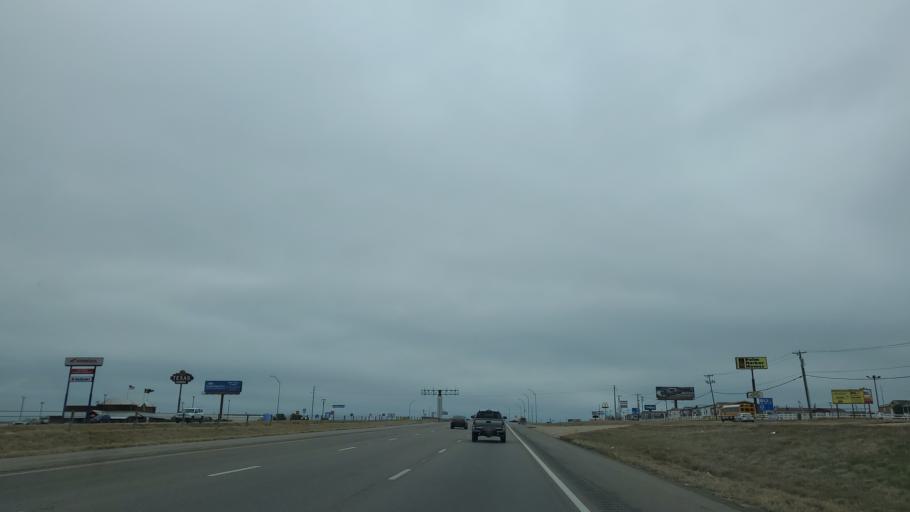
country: US
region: Texas
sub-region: Bell County
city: Killeen
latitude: 31.0831
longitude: -97.7043
